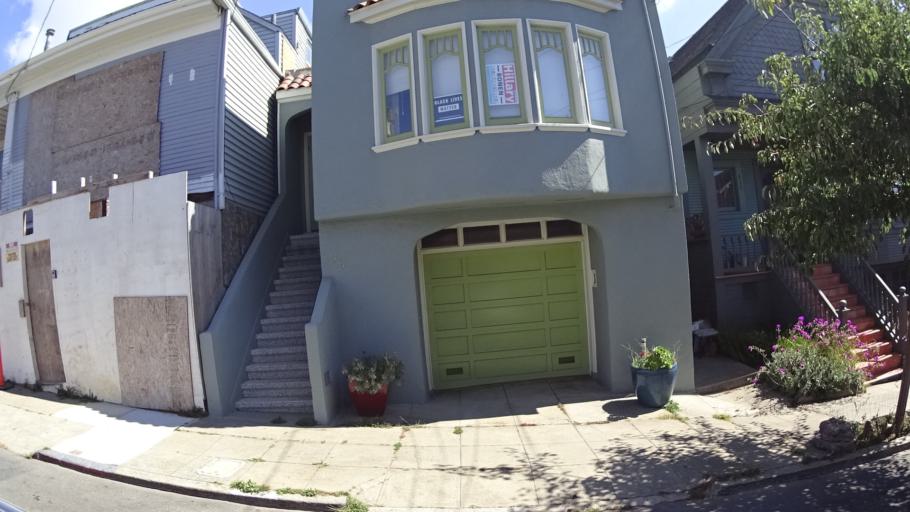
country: US
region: California
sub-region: San Francisco County
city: San Francisco
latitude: 37.7382
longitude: -122.4140
